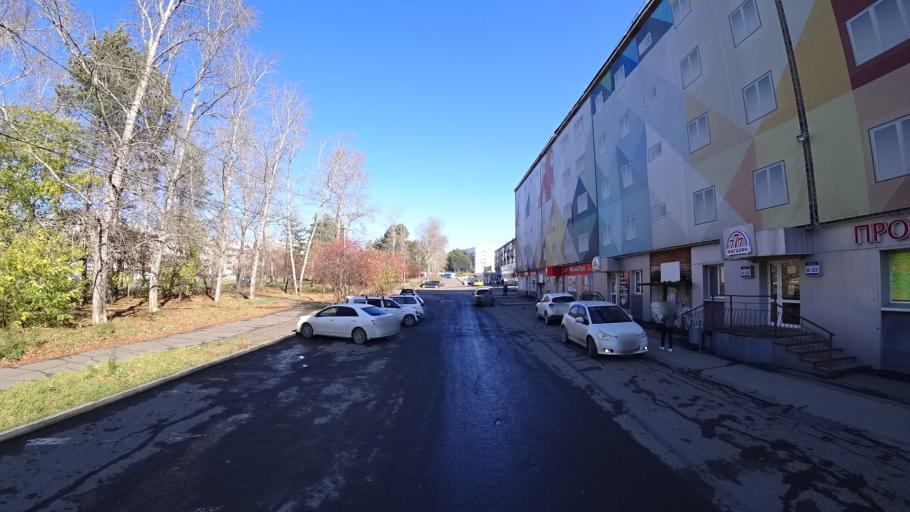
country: RU
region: Khabarovsk Krai
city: Amursk
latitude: 50.2248
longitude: 136.9084
